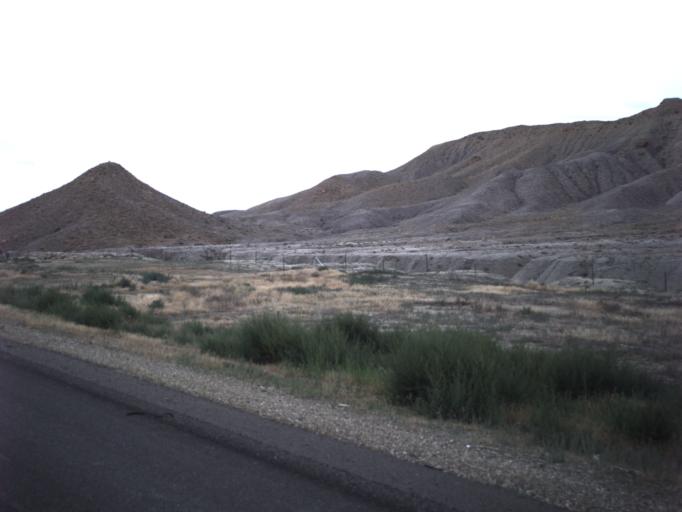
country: US
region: Utah
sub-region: Carbon County
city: East Carbon City
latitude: 39.2932
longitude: -110.3536
